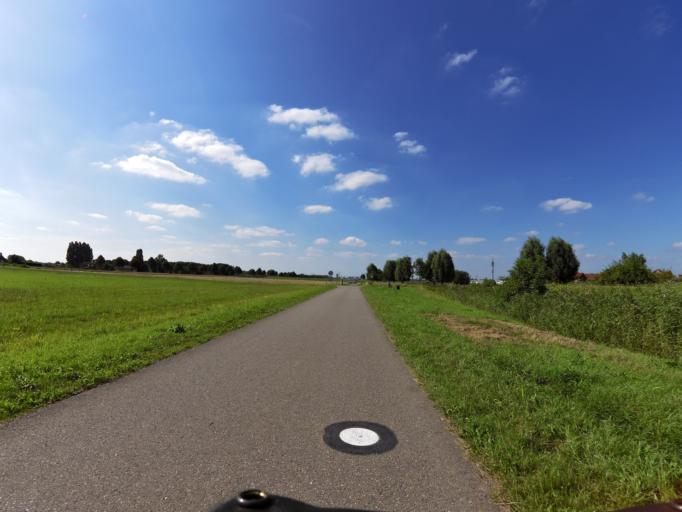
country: NL
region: South Holland
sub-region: Gemeente Binnenmaas
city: Heinenoord
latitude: 51.8544
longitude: 4.4657
